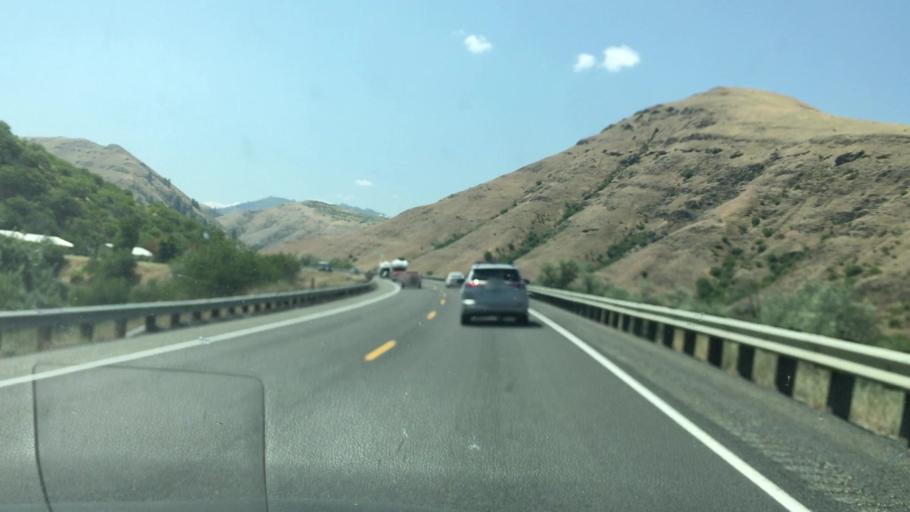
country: US
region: Idaho
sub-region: Idaho County
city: Grangeville
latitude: 45.7233
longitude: -116.3085
